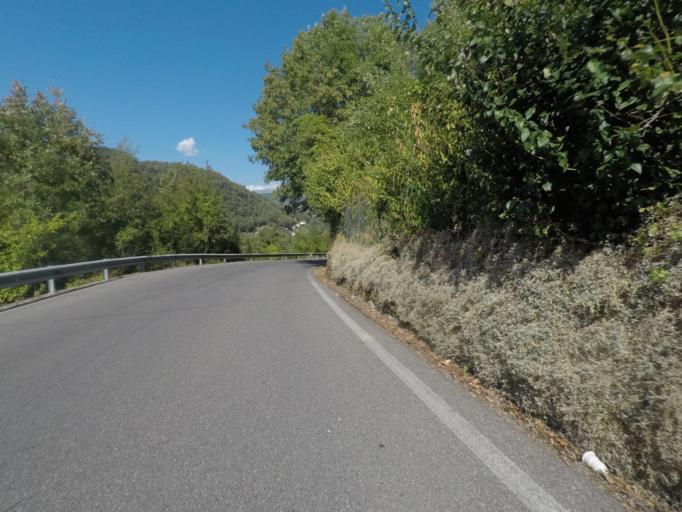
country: IT
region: Tuscany
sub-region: Provincia di Massa-Carrara
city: Pallerone
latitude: 44.1985
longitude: 10.0567
